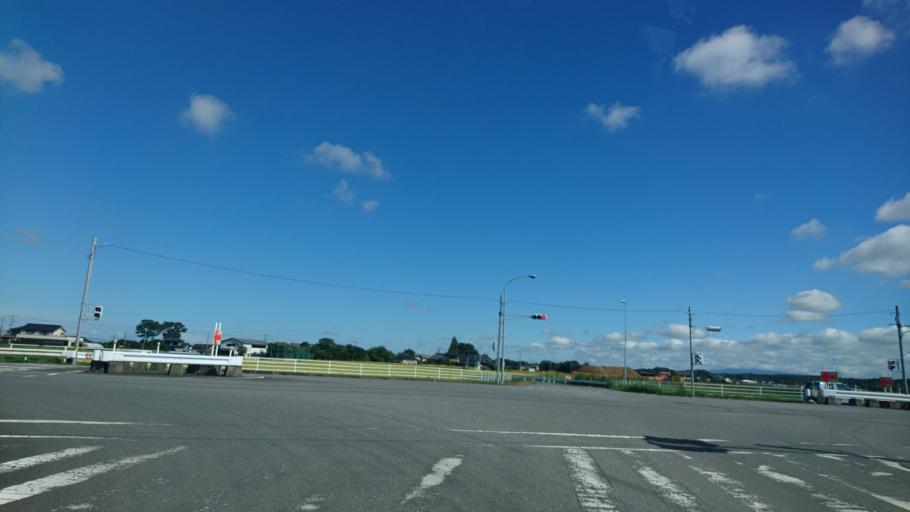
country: JP
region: Ibaraki
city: Mitsukaido
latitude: 36.0373
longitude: 139.9587
